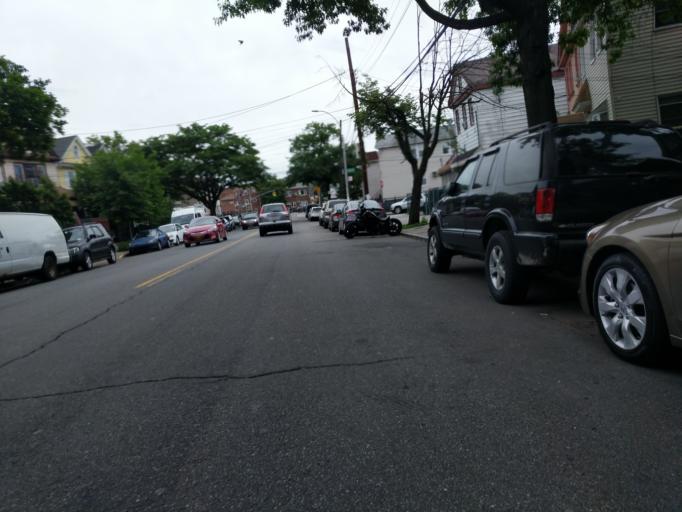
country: US
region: New York
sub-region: Queens County
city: Borough of Queens
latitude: 40.7442
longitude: -73.8655
